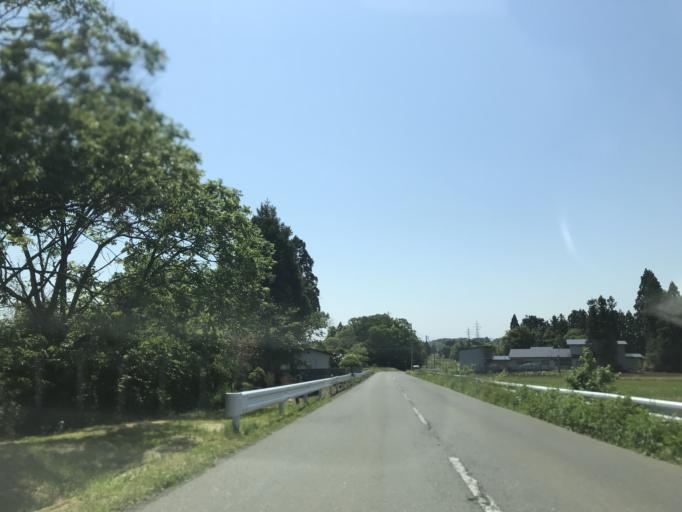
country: JP
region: Iwate
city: Mizusawa
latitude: 39.1896
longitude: 141.0759
